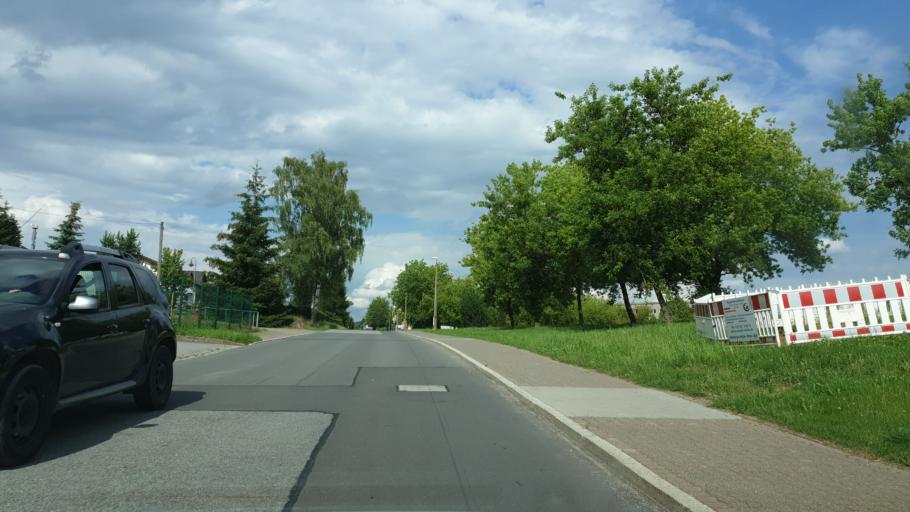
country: DE
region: Saxony
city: Lossnitz
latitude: 50.6138
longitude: 12.7140
